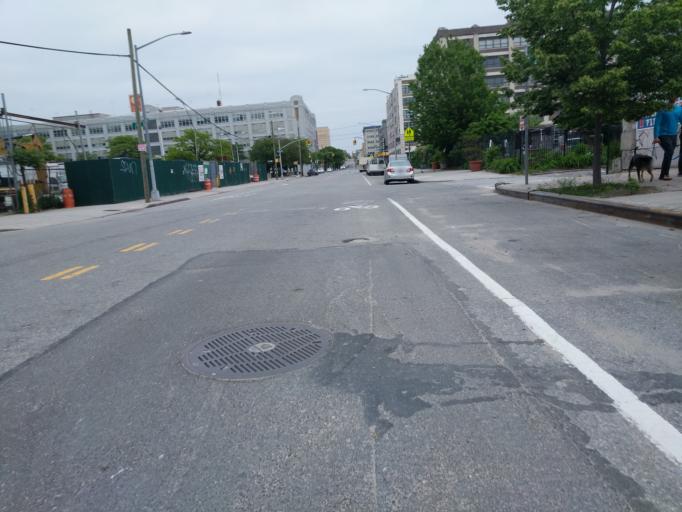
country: US
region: New York
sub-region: Queens County
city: Long Island City
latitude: 40.7434
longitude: -73.9387
